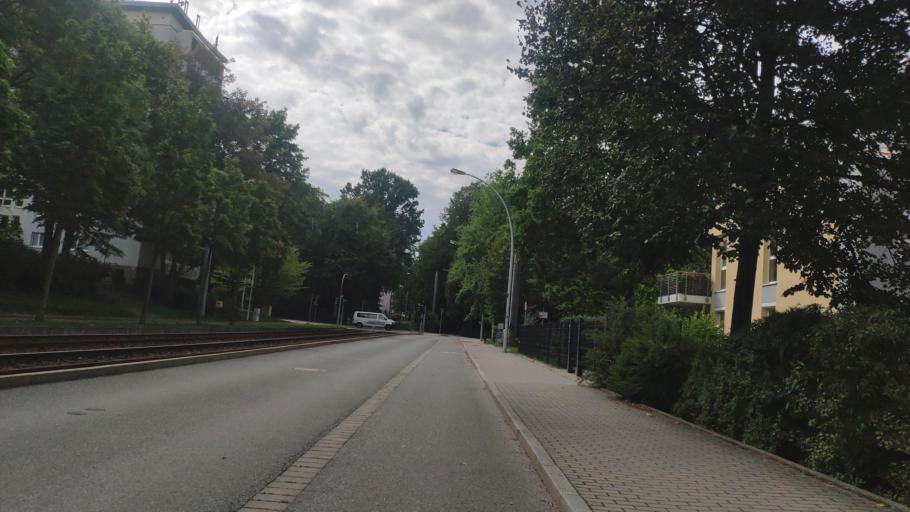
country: DE
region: Saxony
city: Chemnitz
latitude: 50.8230
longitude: 12.9094
